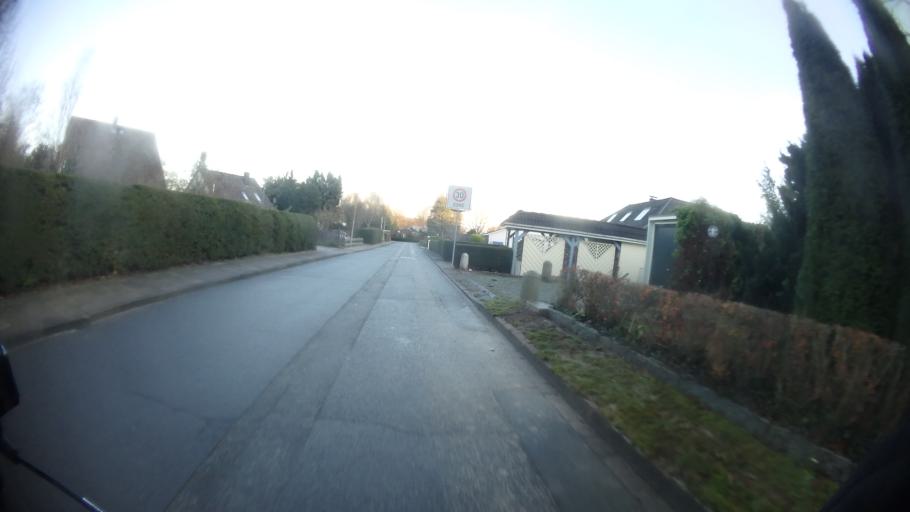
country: DE
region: Schleswig-Holstein
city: Susel
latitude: 54.0196
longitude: 10.7008
